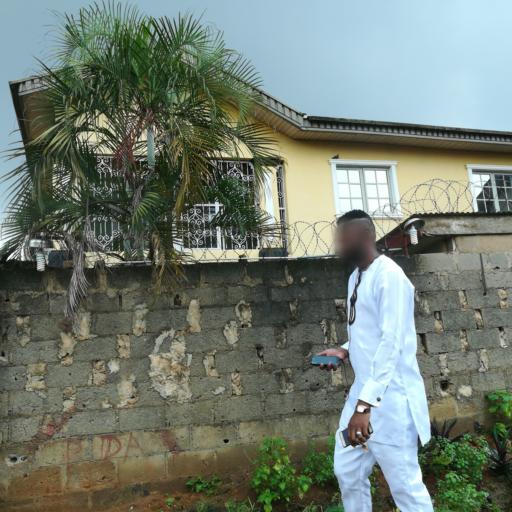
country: NG
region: Lagos
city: Agege
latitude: 6.5918
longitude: 3.2960
